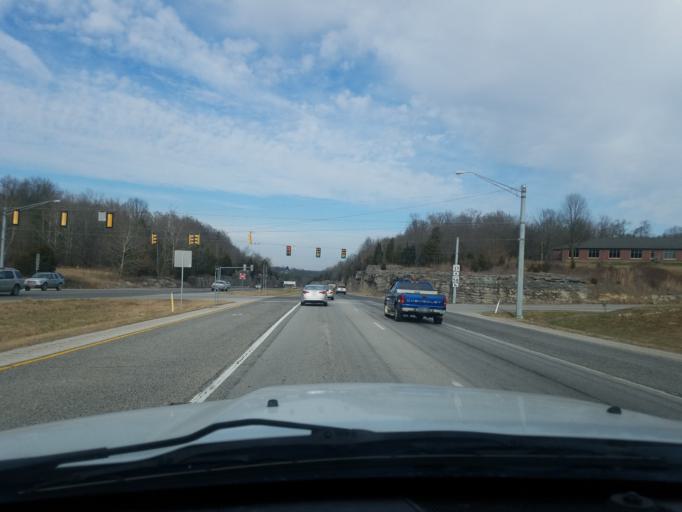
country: US
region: Indiana
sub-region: Lawrence County
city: Oolitic
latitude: 38.8725
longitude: -86.5193
